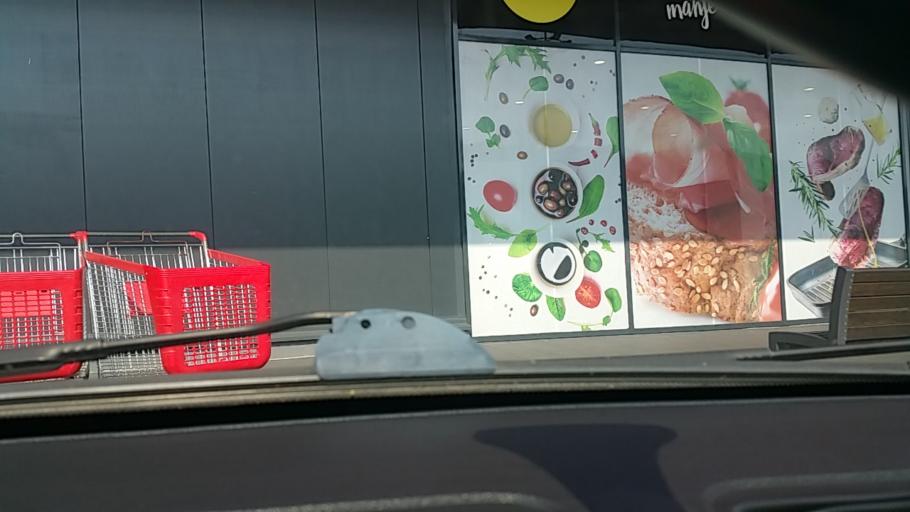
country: RS
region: Central Serbia
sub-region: Belgrade
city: Rakovica
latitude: 44.7399
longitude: 20.4369
